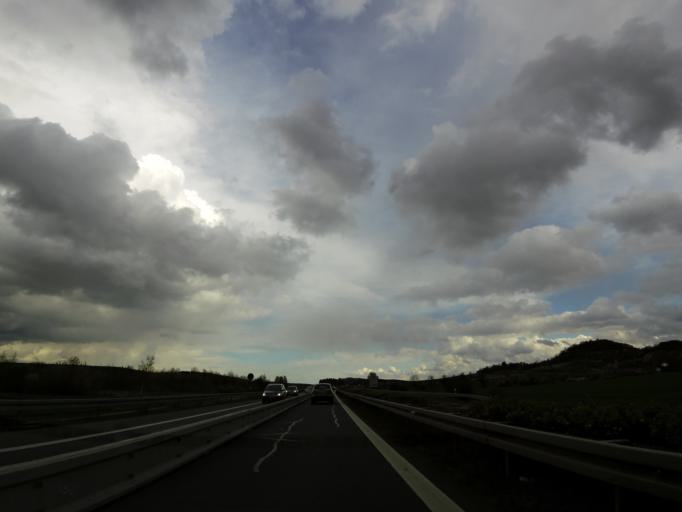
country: DE
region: Saxony-Anhalt
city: Derenburg
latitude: 51.8360
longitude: 10.9053
